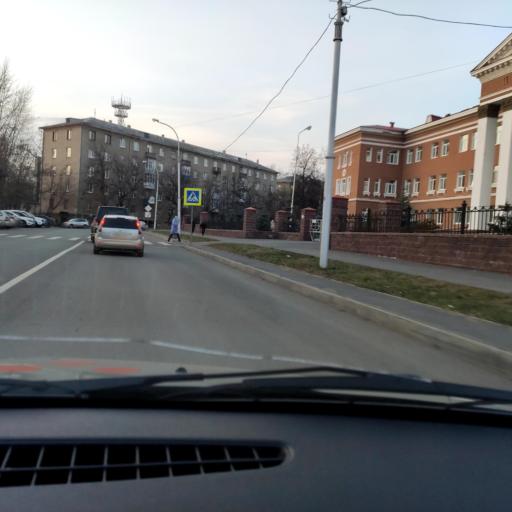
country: RU
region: Bashkortostan
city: Ufa
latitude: 54.8166
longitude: 56.0863
